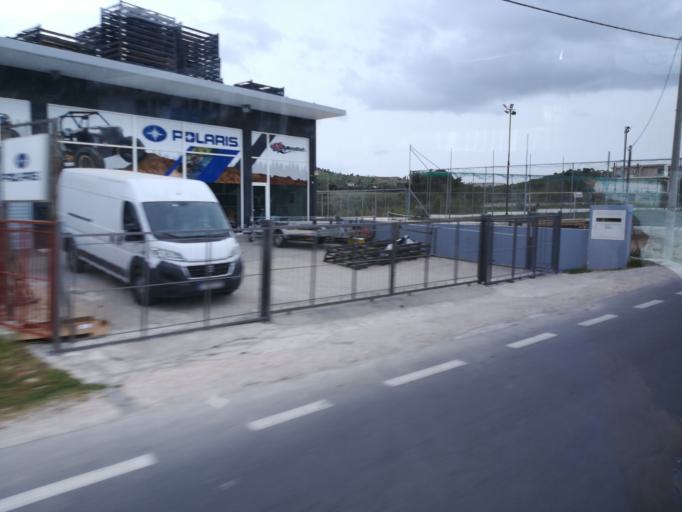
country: GR
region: Attica
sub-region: Nomarchia Anatolikis Attikis
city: Kouvaras
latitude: 37.8203
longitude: 23.9603
